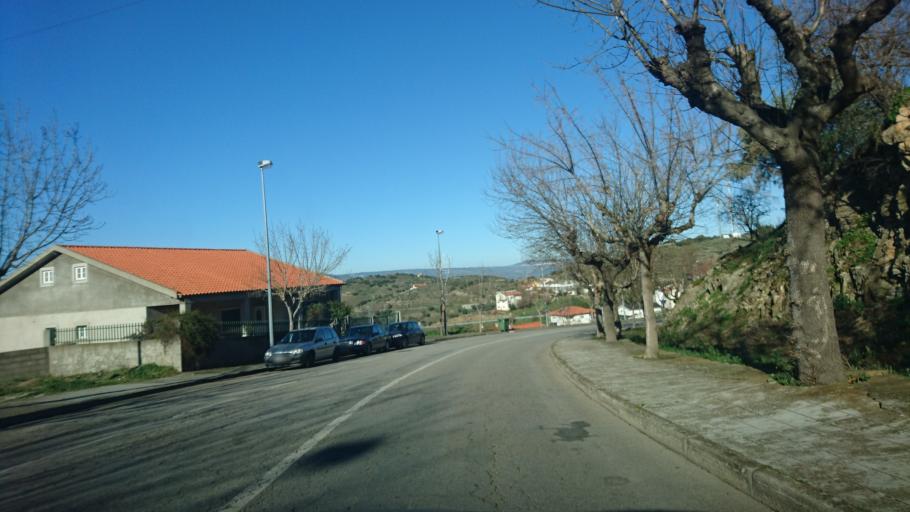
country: PT
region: Braganca
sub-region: Torre de Moncorvo
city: Torre de Moncorvo
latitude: 41.1774
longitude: -7.0538
